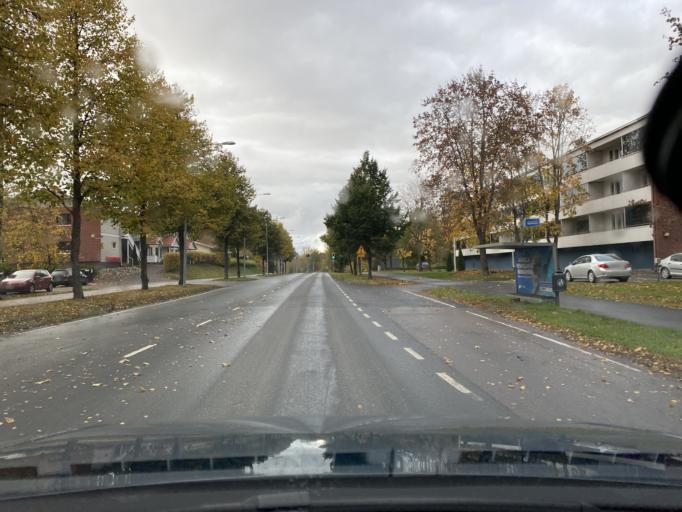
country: FI
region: Haeme
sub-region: Forssa
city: Forssa
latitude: 60.8202
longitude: 23.6083
